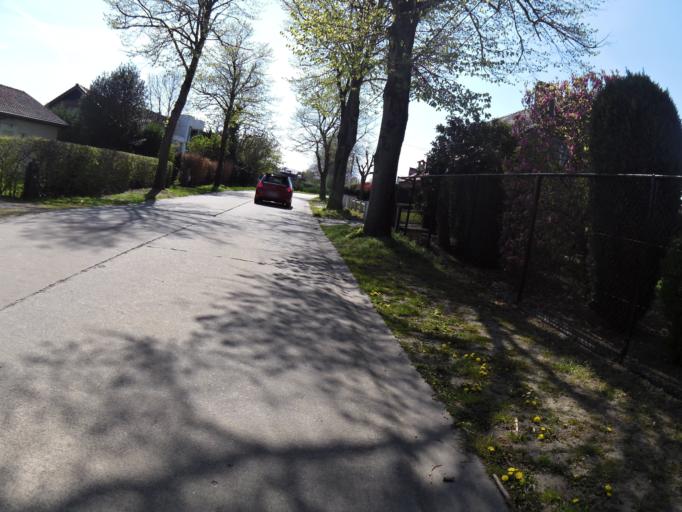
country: BE
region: Flanders
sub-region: Provincie Oost-Vlaanderen
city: Sint-Martens-Latem
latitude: 51.0073
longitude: 3.6275
